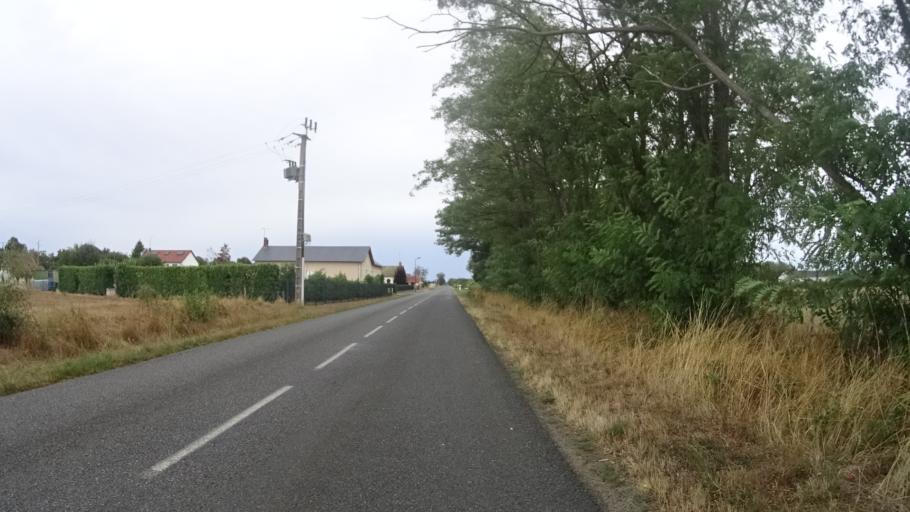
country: FR
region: Bourgogne
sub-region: Departement de la Nievre
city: Lucenay-les-Aix
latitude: 46.7615
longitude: 3.5631
